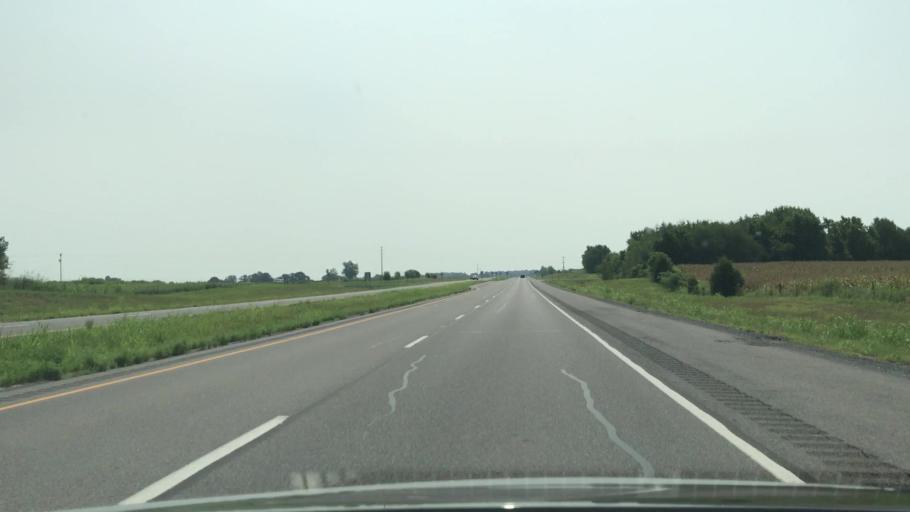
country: US
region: Kentucky
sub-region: Graves County
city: Mayfield
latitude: 36.6874
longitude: -88.5453
